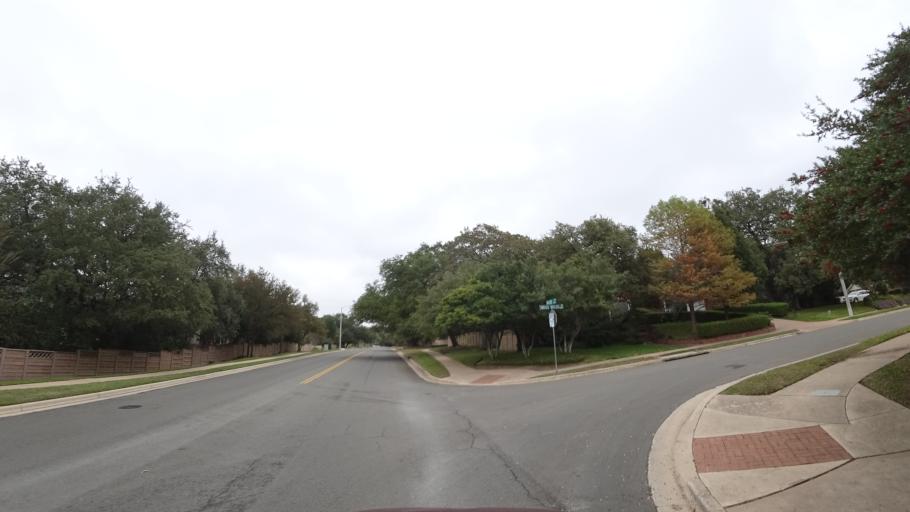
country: US
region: Texas
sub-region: Williamson County
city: Anderson Mill
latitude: 30.4337
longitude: -97.8298
